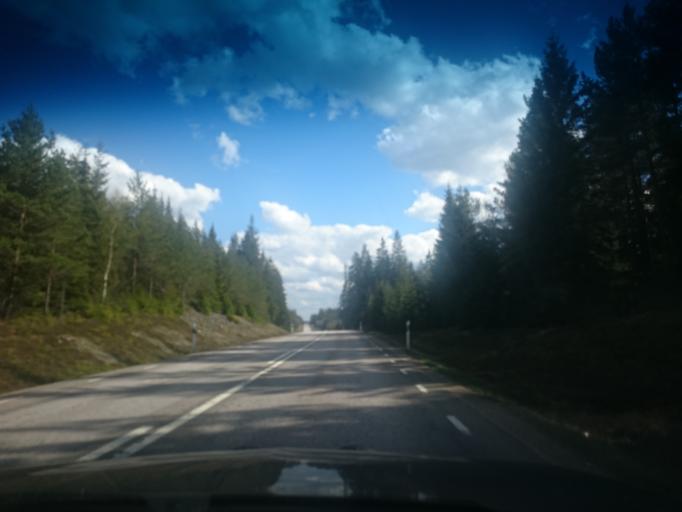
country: SE
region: Joenkoeping
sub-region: Vetlanda Kommun
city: Vetlanda
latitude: 57.2566
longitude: 15.1295
